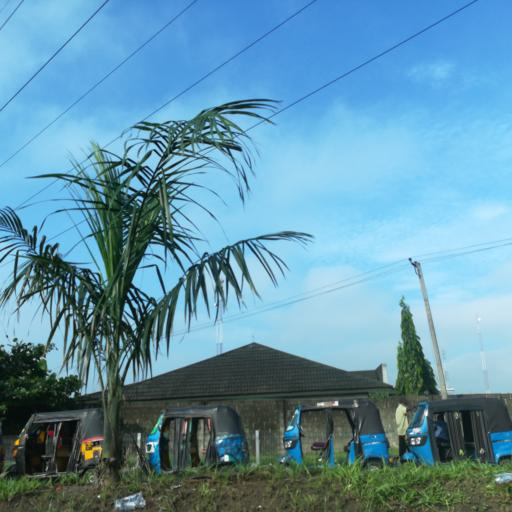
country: NG
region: Rivers
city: Port Harcourt
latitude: 4.8087
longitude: 7.0169
